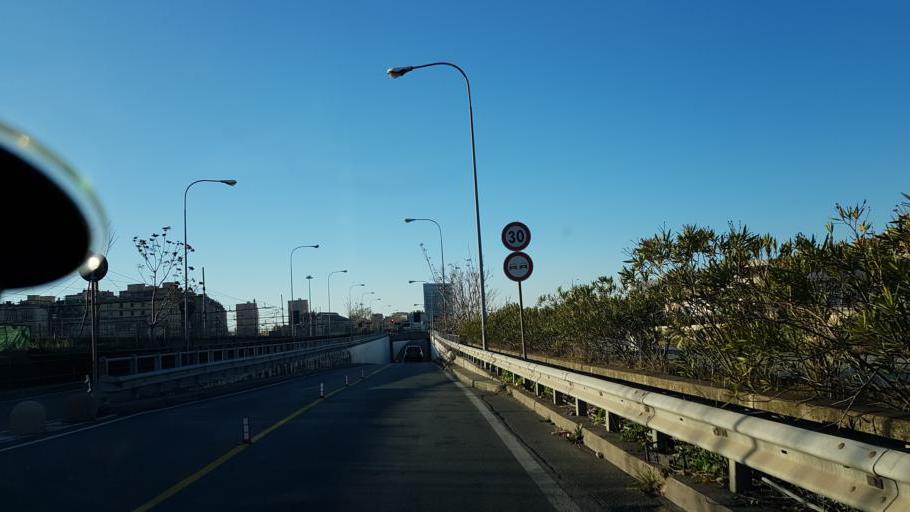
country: IT
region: Liguria
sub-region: Provincia di Genova
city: San Teodoro
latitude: 44.4231
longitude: 8.8865
